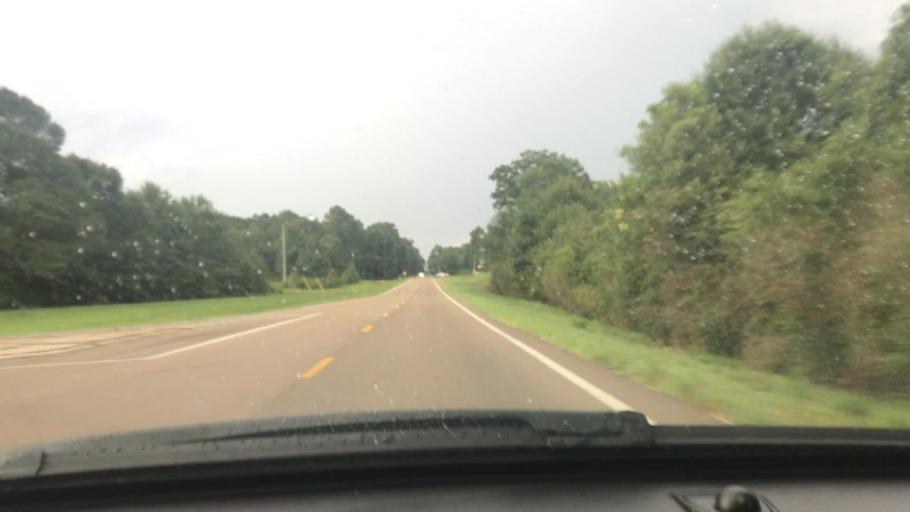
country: US
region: Mississippi
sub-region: Pike County
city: Summit
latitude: 31.3533
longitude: -90.6080
